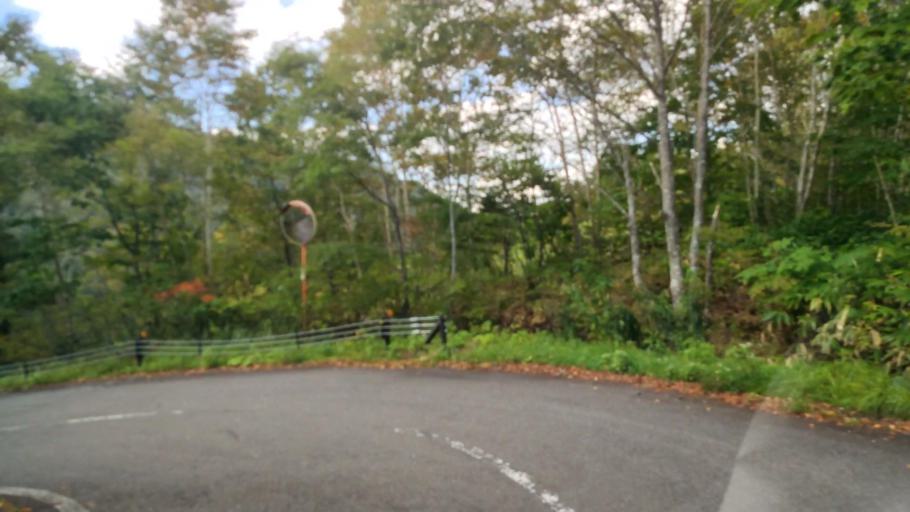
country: JP
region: Gunma
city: Nakanojomachi
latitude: 36.7193
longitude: 138.6448
